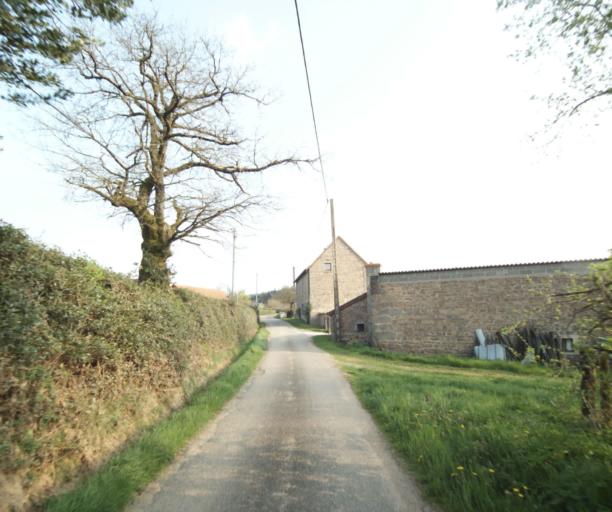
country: FR
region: Bourgogne
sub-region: Departement de Saone-et-Loire
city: Matour
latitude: 46.4232
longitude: 4.4827
